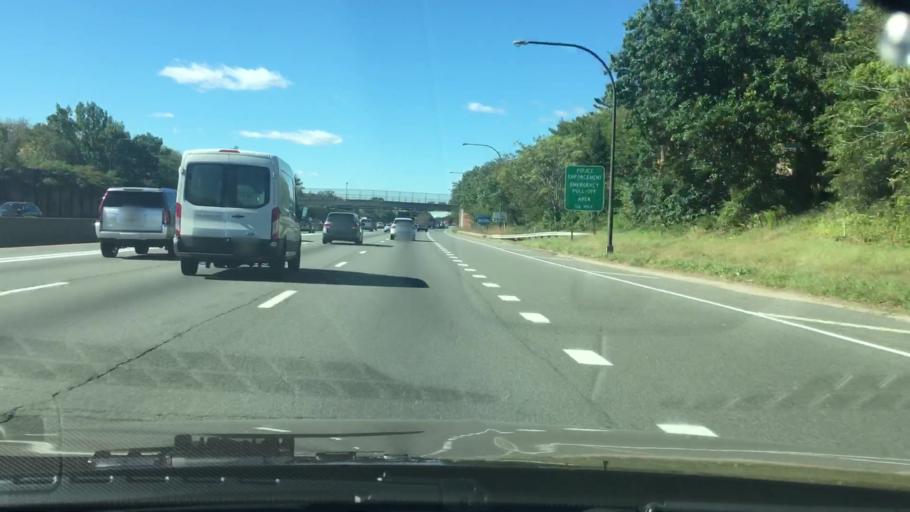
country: US
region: New York
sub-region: Nassau County
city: Jericho
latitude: 40.7844
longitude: -73.5390
